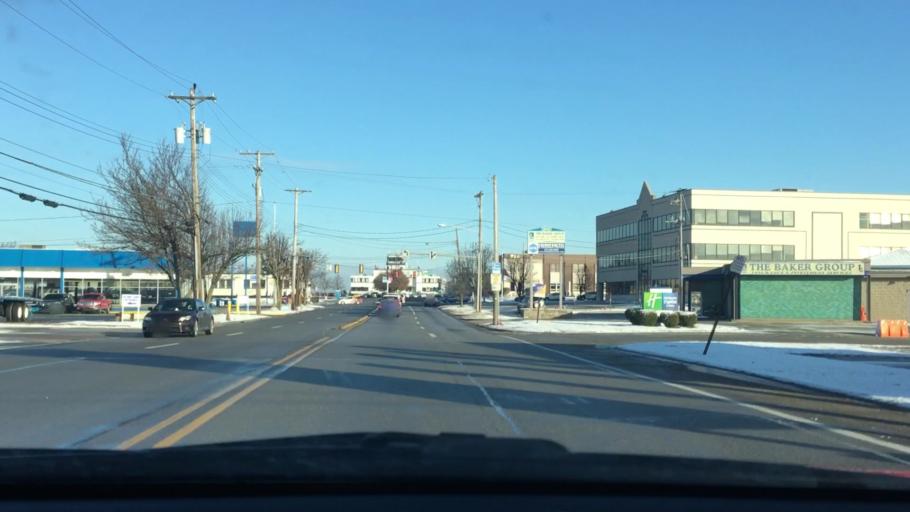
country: US
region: Pennsylvania
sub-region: Allegheny County
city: Pleasant Hills
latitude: 40.3490
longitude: -79.9271
